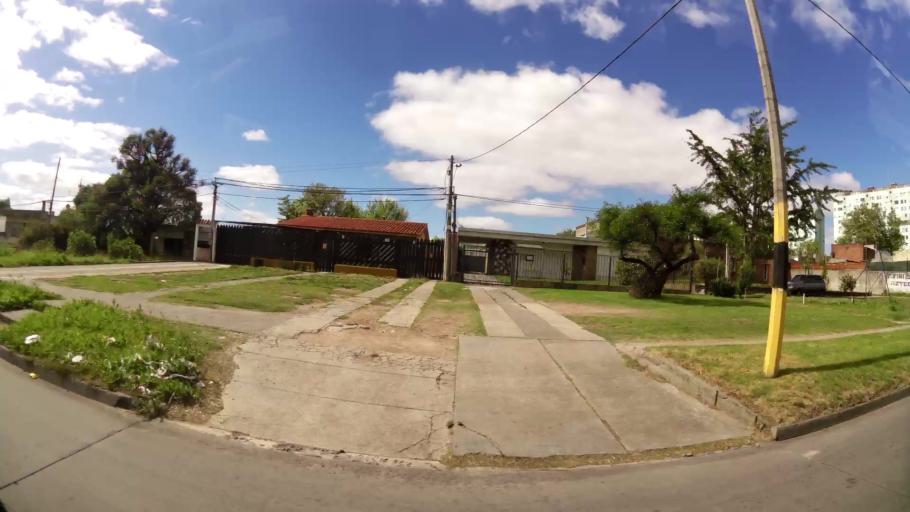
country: UY
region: Canelones
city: Paso de Carrasco
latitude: -34.8709
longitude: -56.1148
